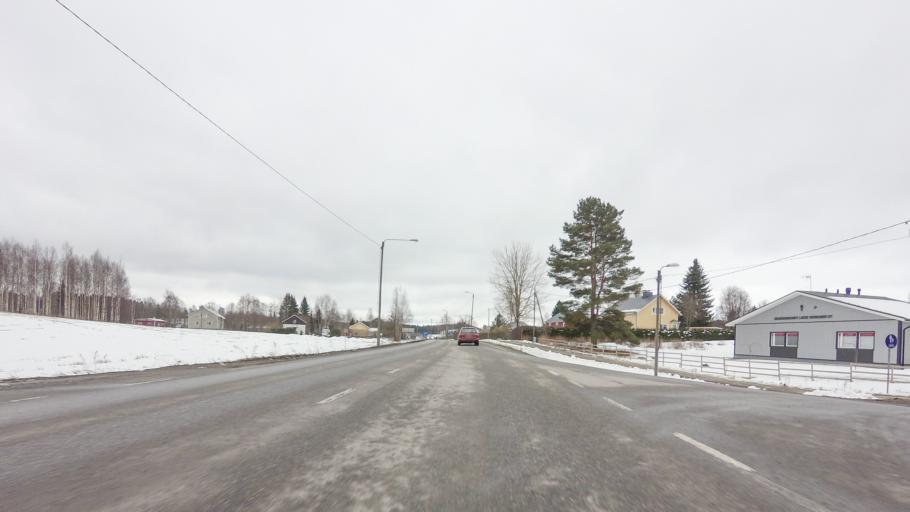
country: FI
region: Southern Savonia
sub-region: Savonlinna
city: Savonlinna
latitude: 61.8786
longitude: 28.9475
